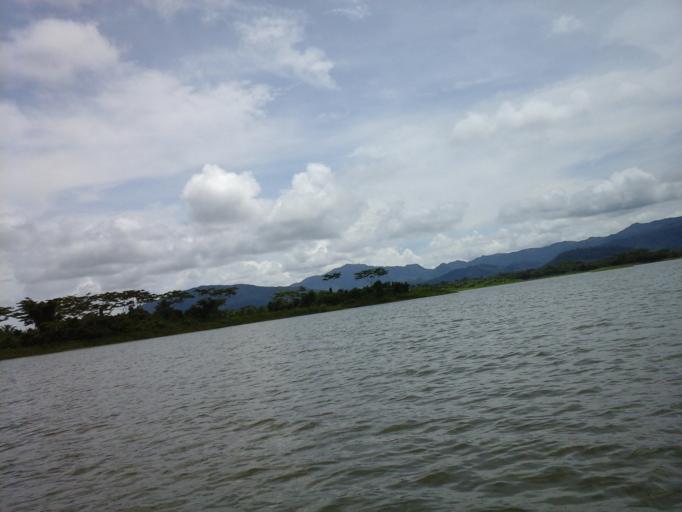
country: CO
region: Bolivar
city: San Cristobal
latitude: 9.8764
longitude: -75.3027
